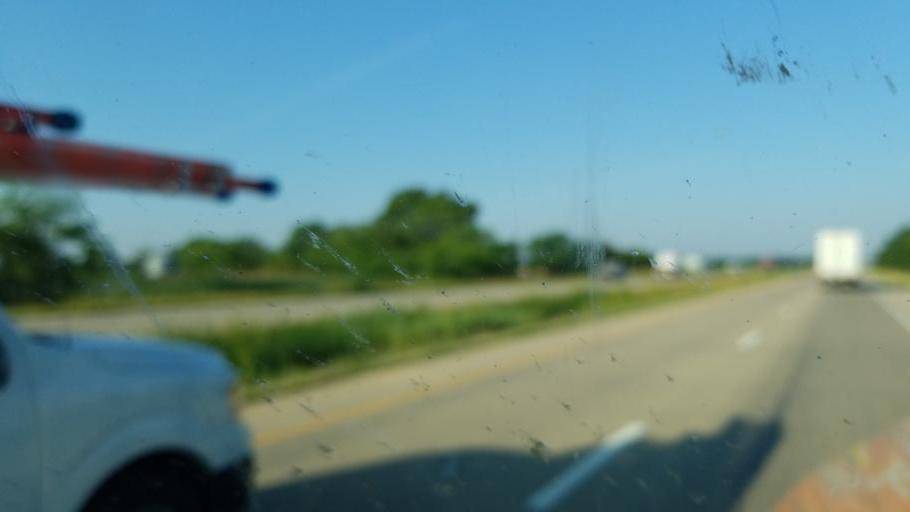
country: US
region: Illinois
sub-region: Grundy County
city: Morris
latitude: 41.4107
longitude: -88.3834
